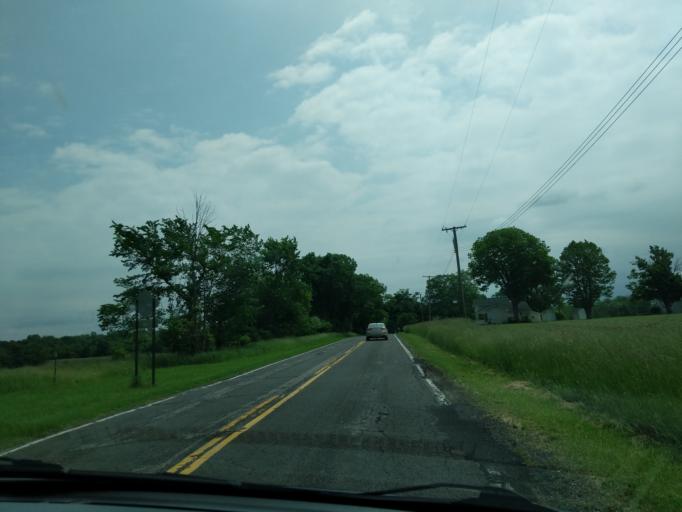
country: US
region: Michigan
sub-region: Ingham County
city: Williamston
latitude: 42.6935
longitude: -84.2473
